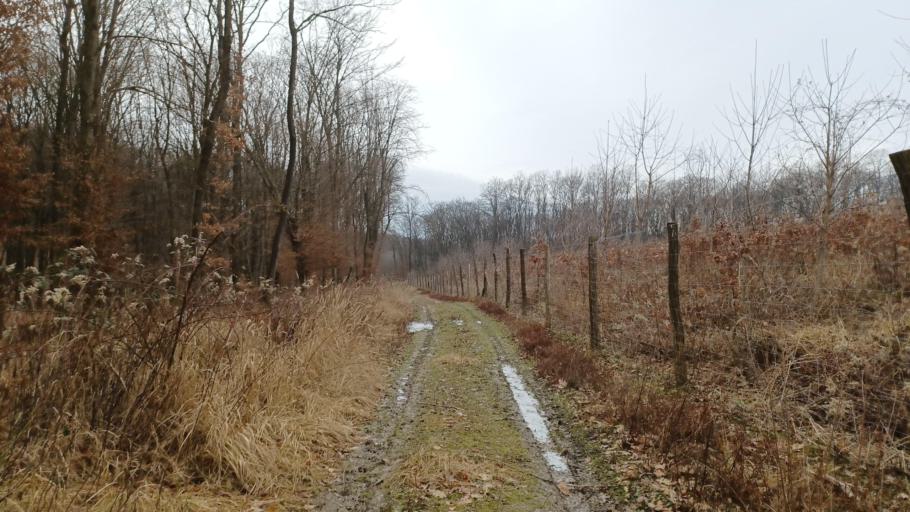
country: HU
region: Tolna
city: Szentgalpuszta
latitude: 46.3060
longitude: 18.6403
